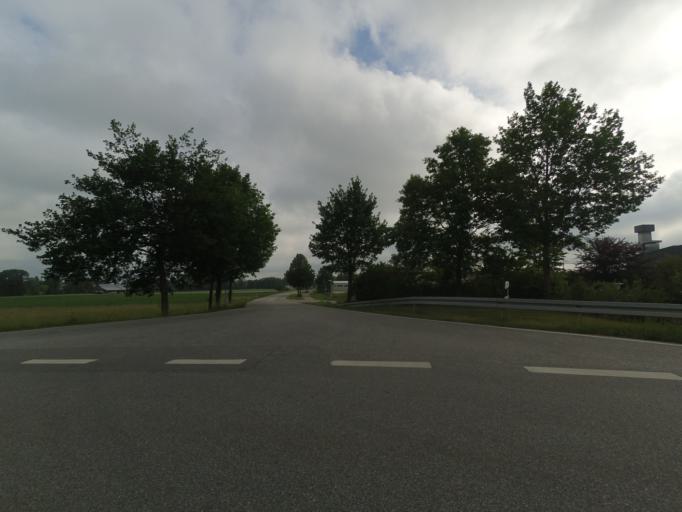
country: DE
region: Bavaria
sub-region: Lower Bavaria
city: Perkam
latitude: 48.8606
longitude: 12.4431
